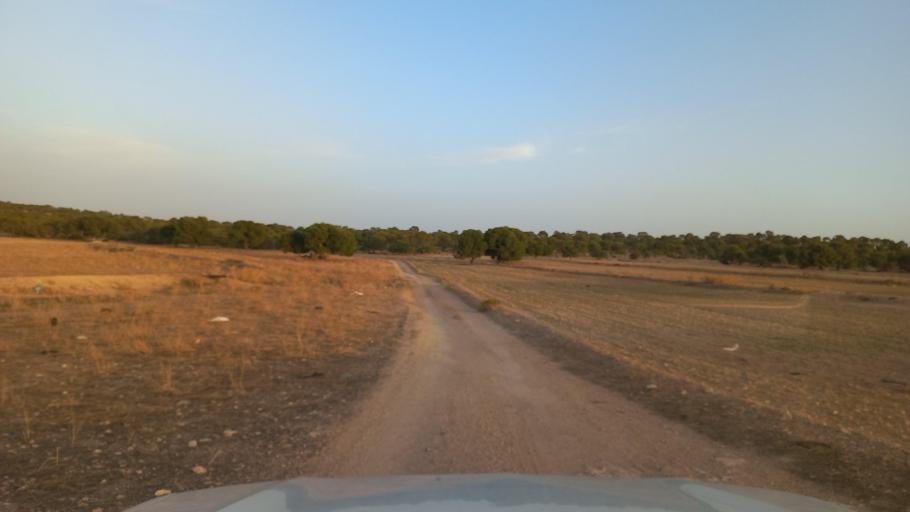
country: TN
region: Al Qasrayn
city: Sbiba
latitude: 35.4257
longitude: 8.9150
